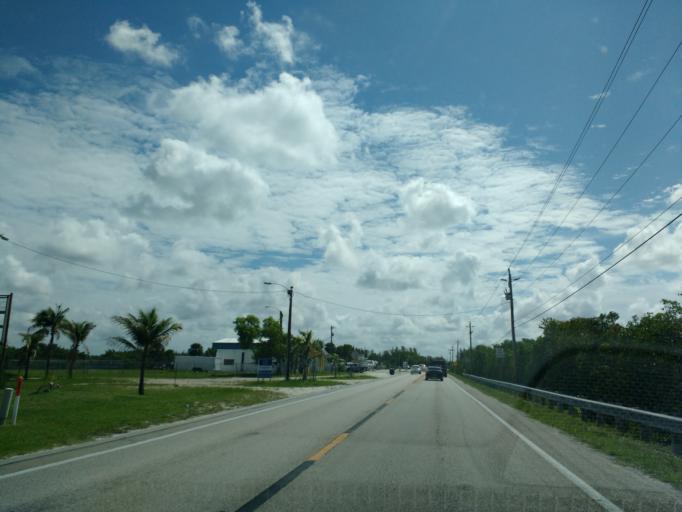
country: US
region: Florida
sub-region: Lee County
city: Pine Island Center
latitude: 26.6383
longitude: -82.0604
